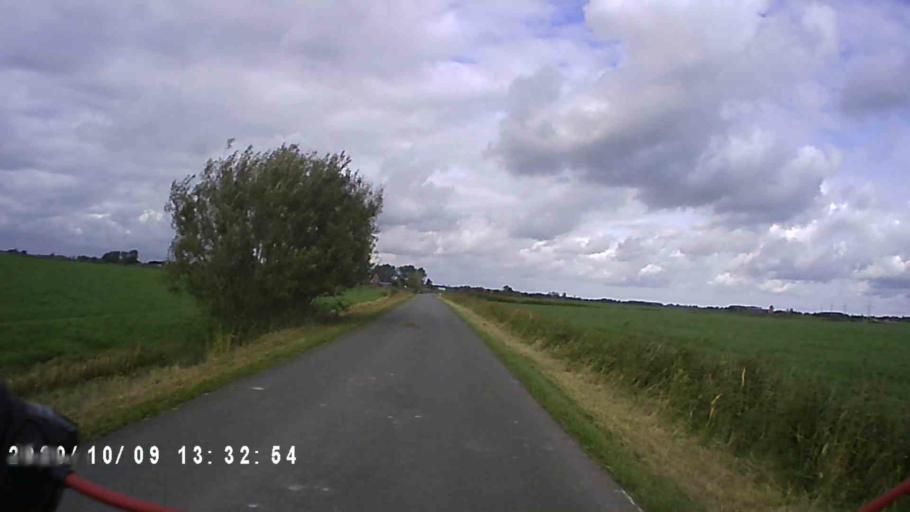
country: NL
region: Groningen
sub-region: Gemeente Zuidhorn
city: Aduard
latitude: 53.2869
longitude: 6.4734
